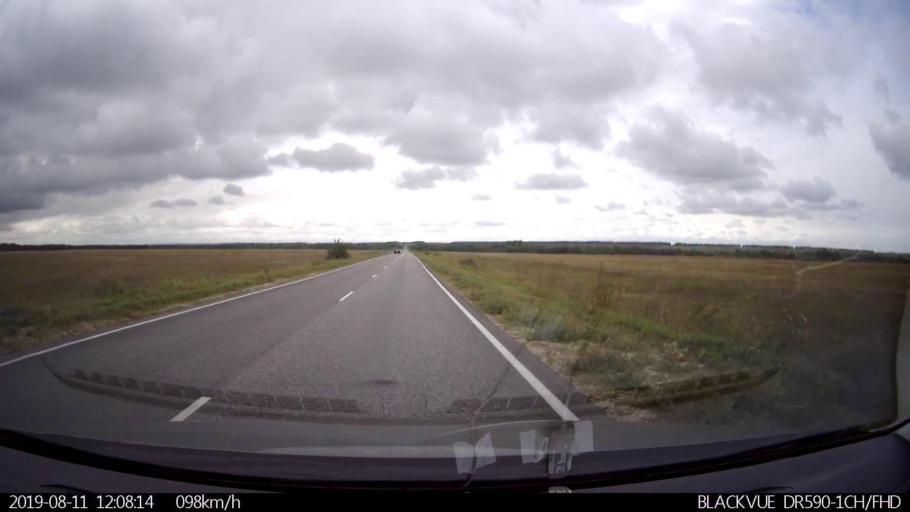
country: RU
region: Ulyanovsk
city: Silikatnyy
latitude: 53.9952
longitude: 48.0757
